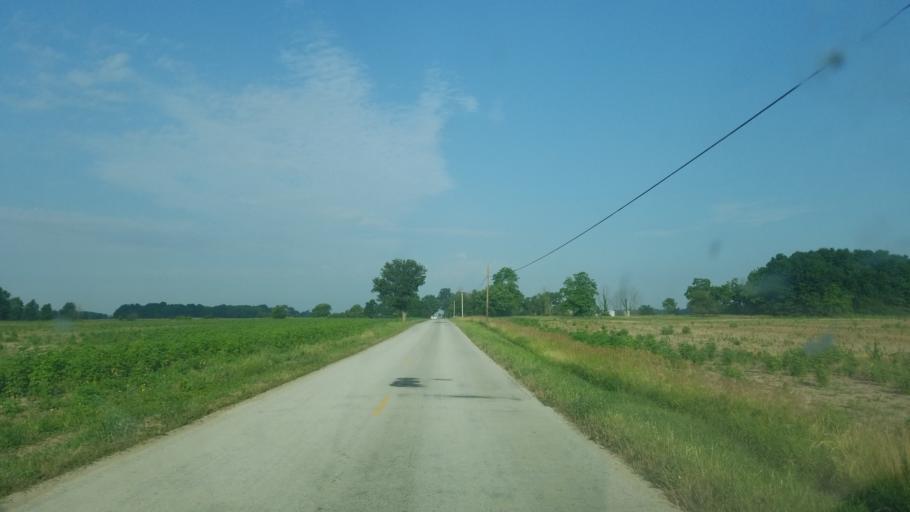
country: US
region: Ohio
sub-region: Hardin County
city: Kenton
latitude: 40.6291
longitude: -83.6860
